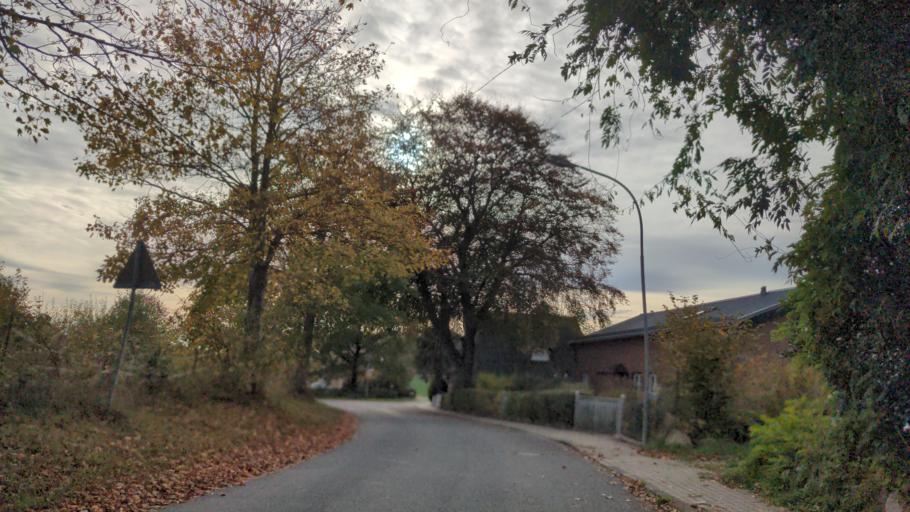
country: DE
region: Schleswig-Holstein
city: Bosdorf
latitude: 54.1291
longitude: 10.5001
